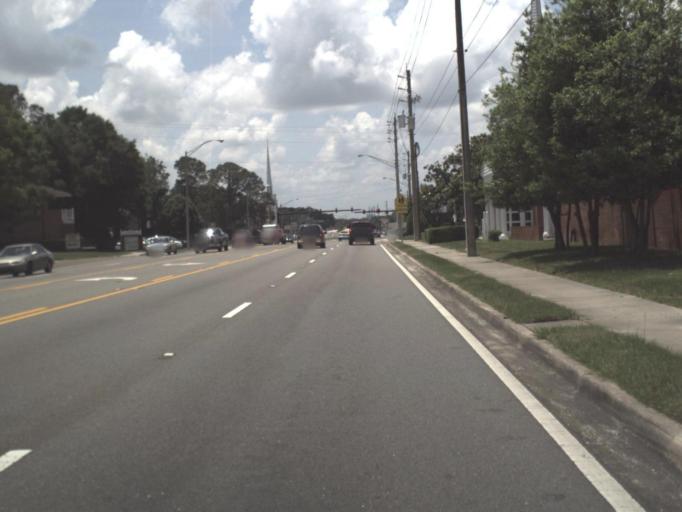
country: US
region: Florida
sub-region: Duval County
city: Jacksonville
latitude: 30.2777
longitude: -81.7284
